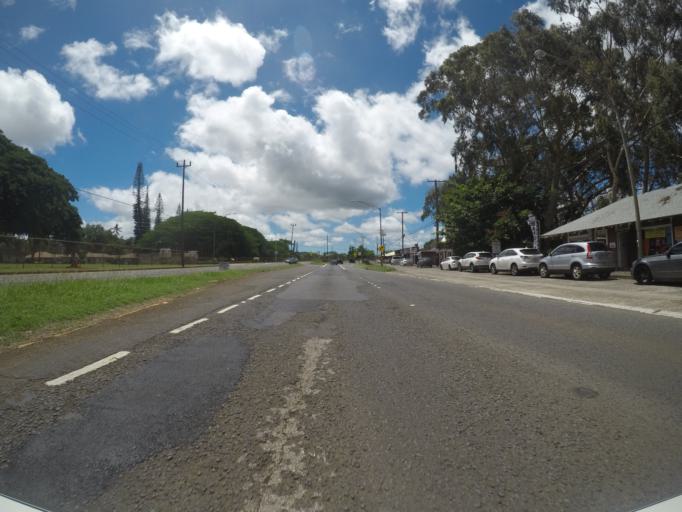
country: US
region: Hawaii
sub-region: Honolulu County
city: Schofield Barracks
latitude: 21.4940
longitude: -158.0495
